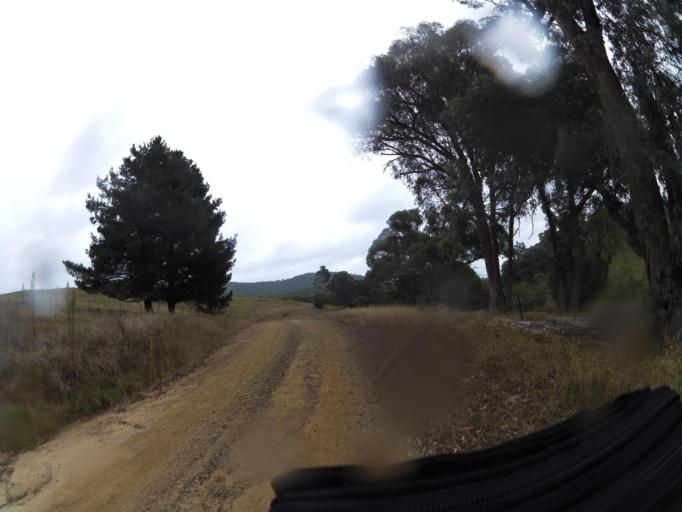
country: AU
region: New South Wales
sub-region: Greater Hume Shire
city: Holbrook
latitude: -36.2363
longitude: 147.6185
